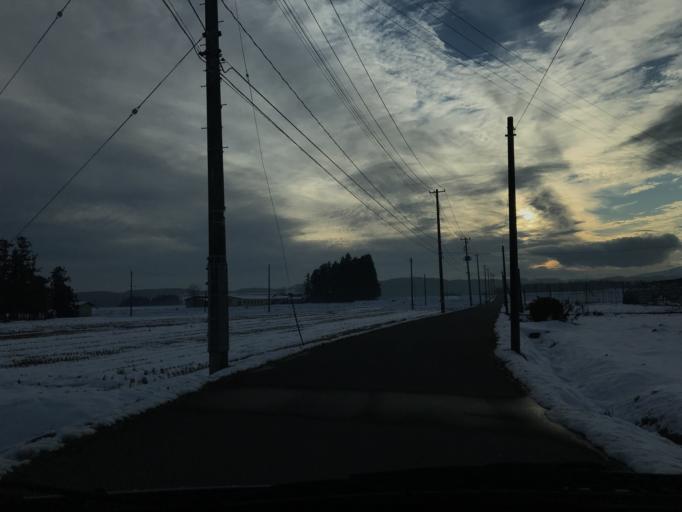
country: JP
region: Iwate
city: Mizusawa
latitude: 39.0629
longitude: 141.0932
